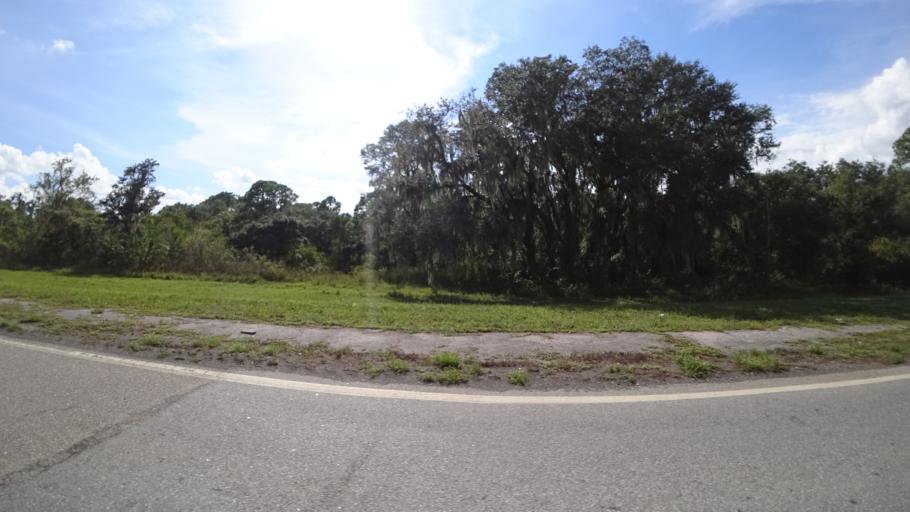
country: US
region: Florida
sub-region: Hillsborough County
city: Wimauma
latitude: 27.5386
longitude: -82.1033
